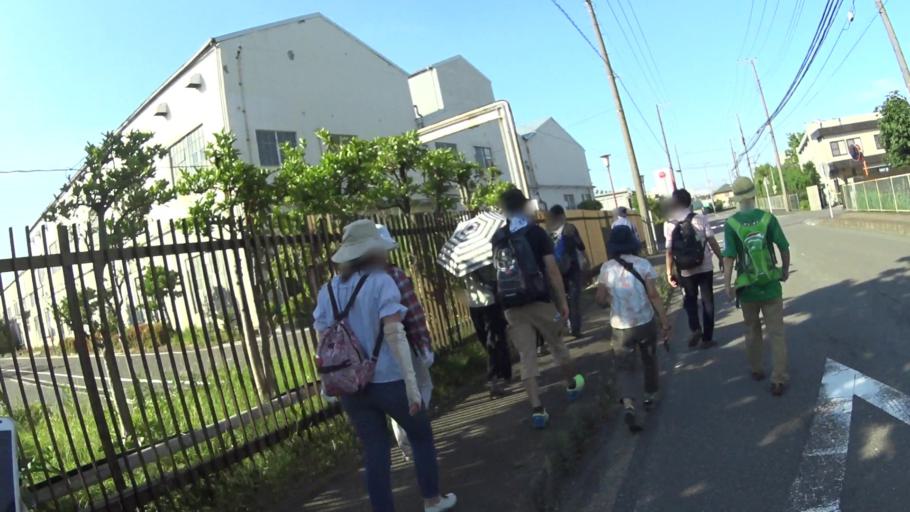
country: JP
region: Kanagawa
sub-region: Kawasaki-shi
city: Kawasaki
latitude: 35.4993
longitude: 139.6968
